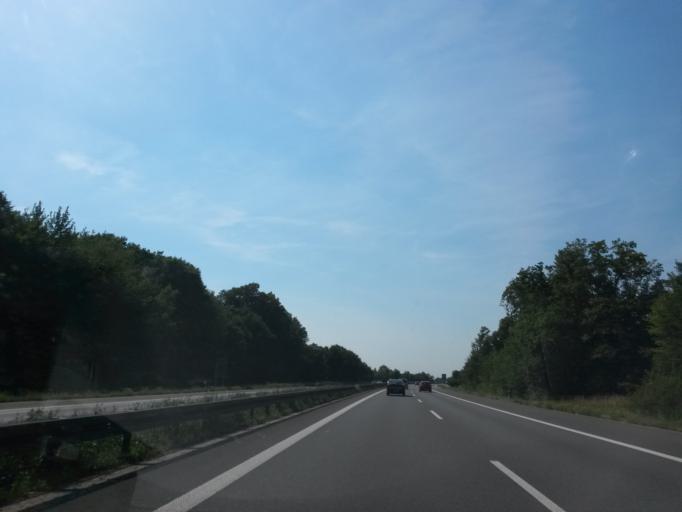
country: DE
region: Bavaria
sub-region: Regierungsbezirk Unterfranken
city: Kleinlangheim
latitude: 49.7757
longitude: 10.3103
